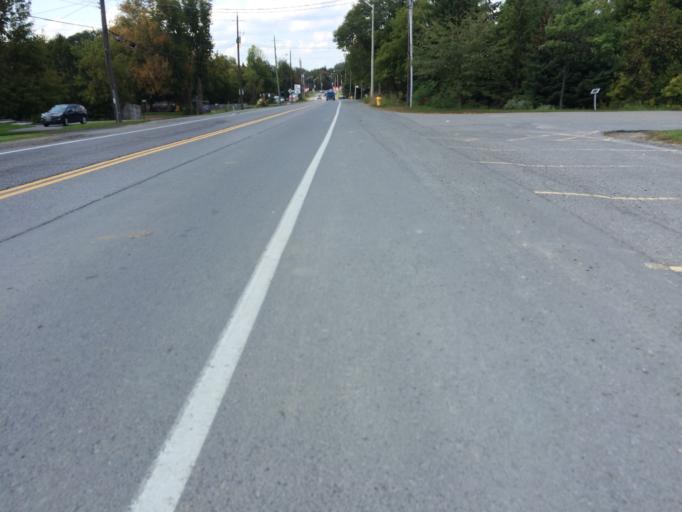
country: CA
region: Ontario
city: Bells Corners
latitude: 45.2193
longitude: -75.6745
